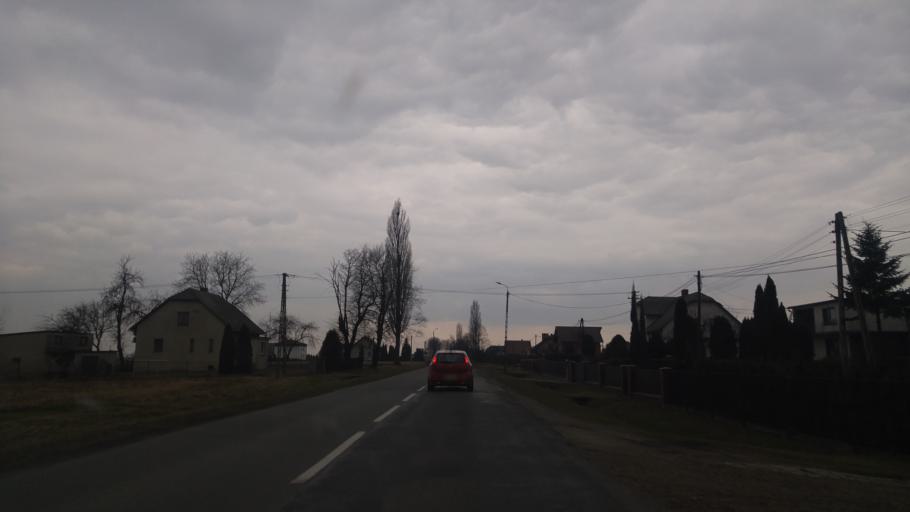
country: PL
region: Silesian Voivodeship
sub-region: Powiat cieszynski
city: Chybie
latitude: 49.9477
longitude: 18.8437
